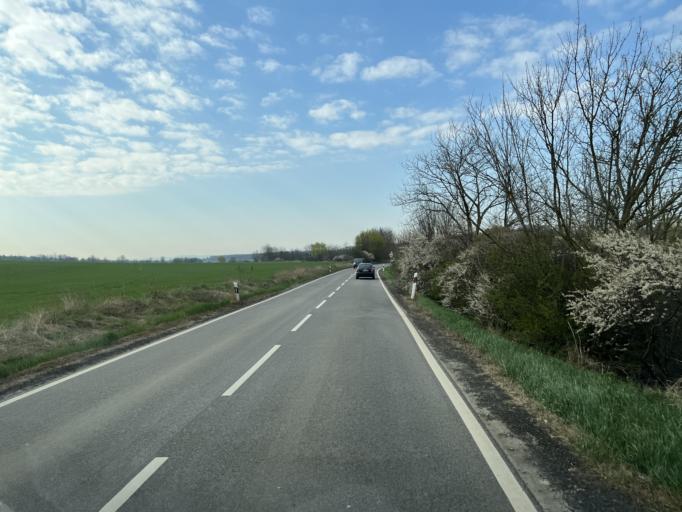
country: HU
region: Pest
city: Acsa
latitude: 47.7569
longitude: 19.3683
